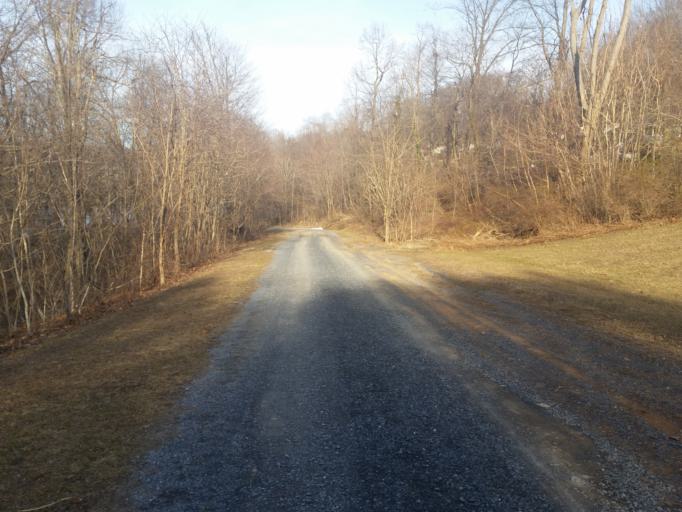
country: US
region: Pennsylvania
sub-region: Perry County
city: Marysville
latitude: 40.3346
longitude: -76.9330
